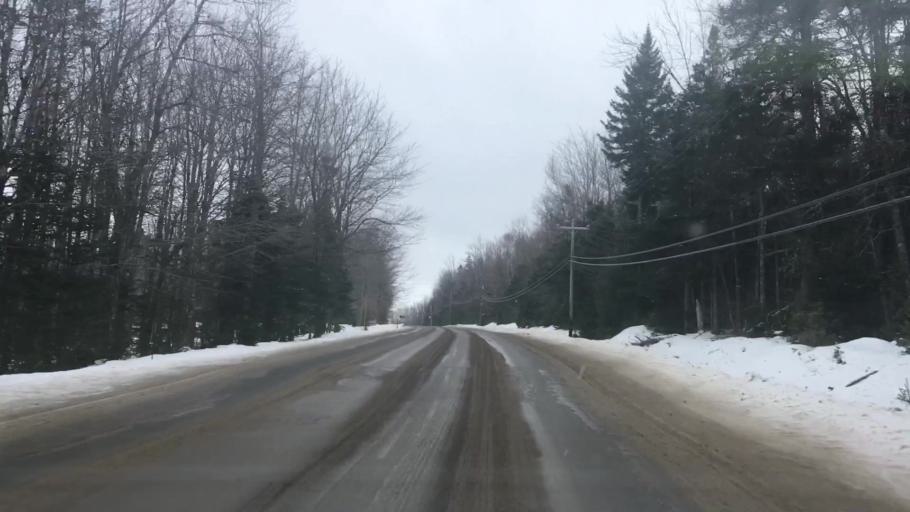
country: US
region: Maine
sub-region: Washington County
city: East Machias
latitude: 44.9902
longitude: -67.4601
